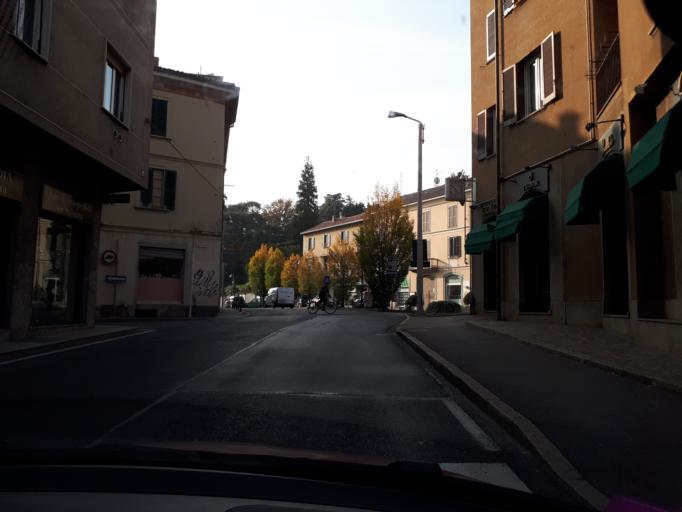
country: IT
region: Lombardy
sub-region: Provincia di Lecco
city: Casatenovo
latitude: 45.6975
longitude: 9.3123
